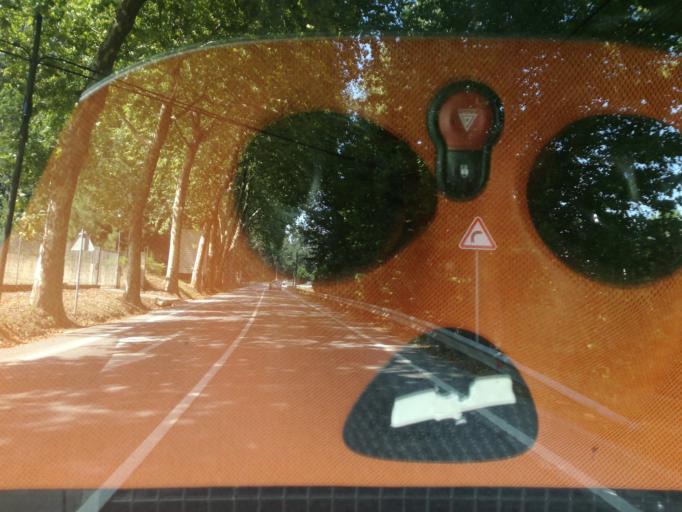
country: PT
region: Braga
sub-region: Esposende
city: Marinhas
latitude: 41.6176
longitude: -8.7770
